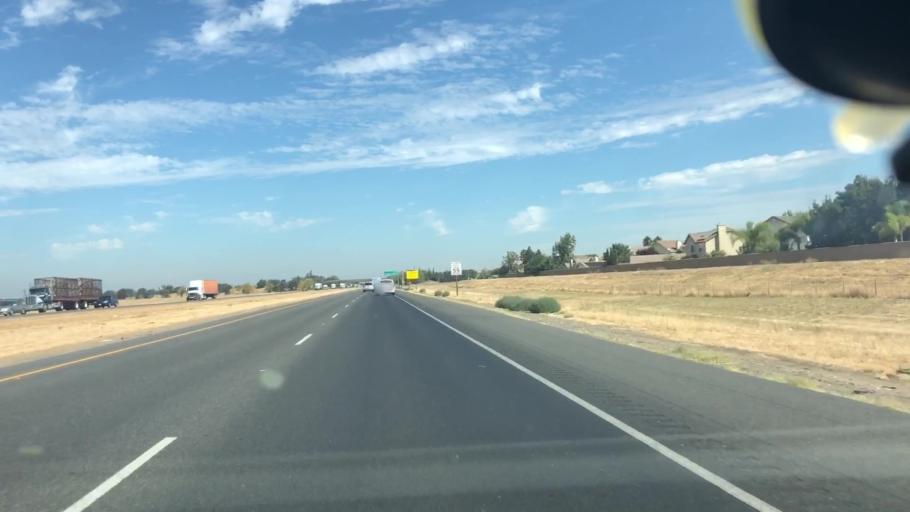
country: US
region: California
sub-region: Sacramento County
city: Laguna
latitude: 38.4012
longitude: -121.4818
